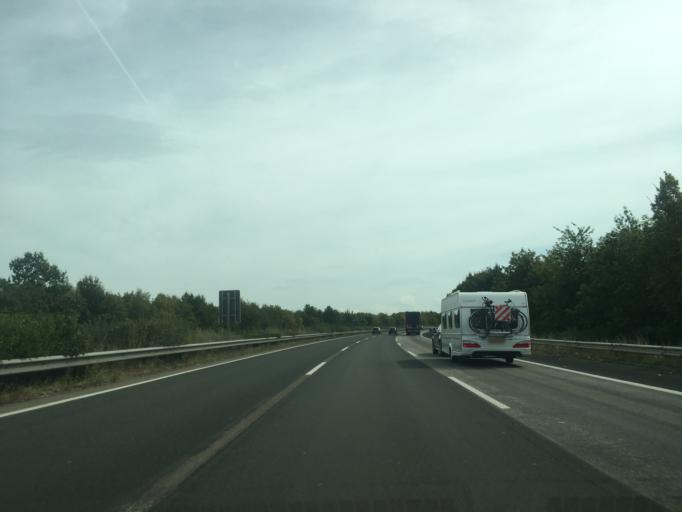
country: DE
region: Rheinland-Pfalz
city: Winningen
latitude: 50.2972
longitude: 7.5035
